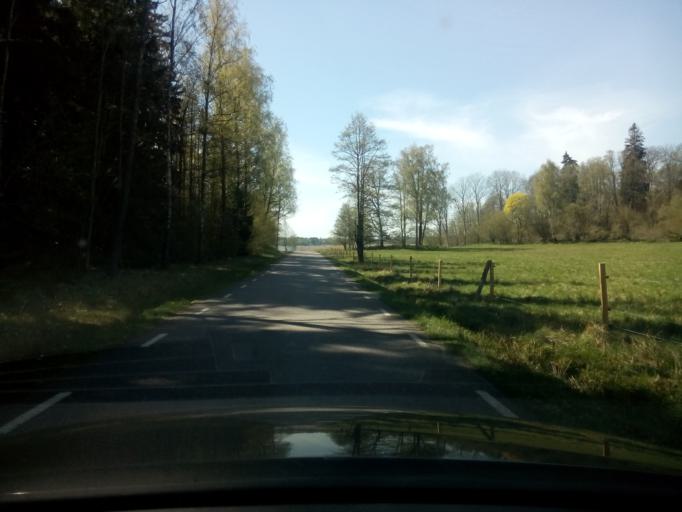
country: SE
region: Soedermanland
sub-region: Trosa Kommun
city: Trosa
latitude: 58.8010
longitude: 17.3700
